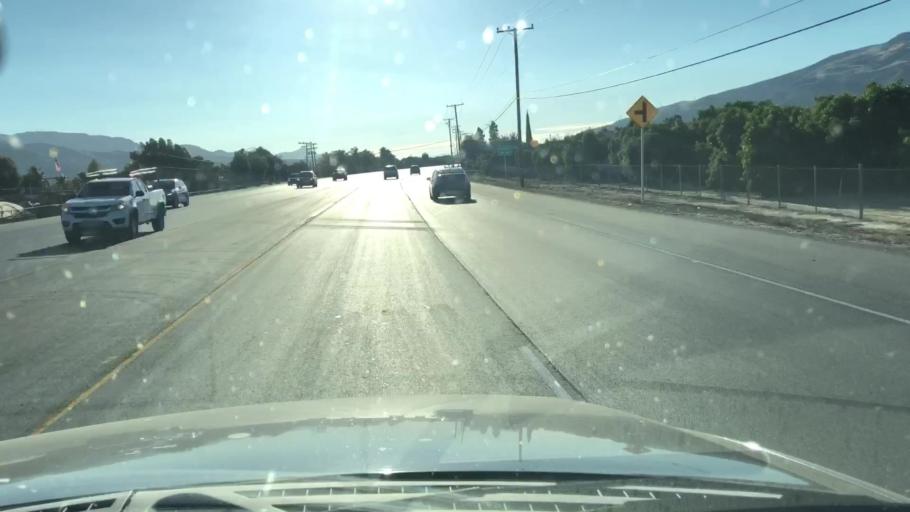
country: US
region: California
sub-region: Ventura County
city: Piru
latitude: 34.4017
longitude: -118.8031
